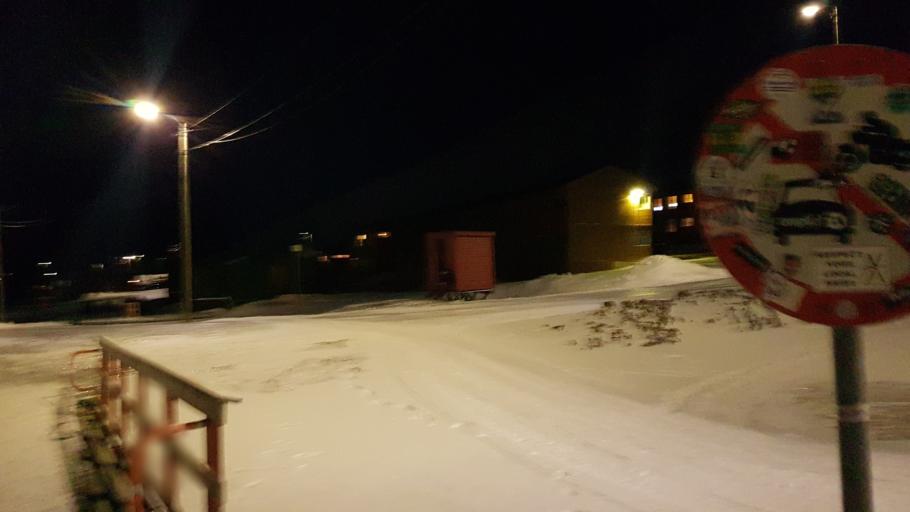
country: SJ
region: Svalbard
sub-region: Spitsbergen
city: Longyearbyen
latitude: 78.2138
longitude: 15.6247
